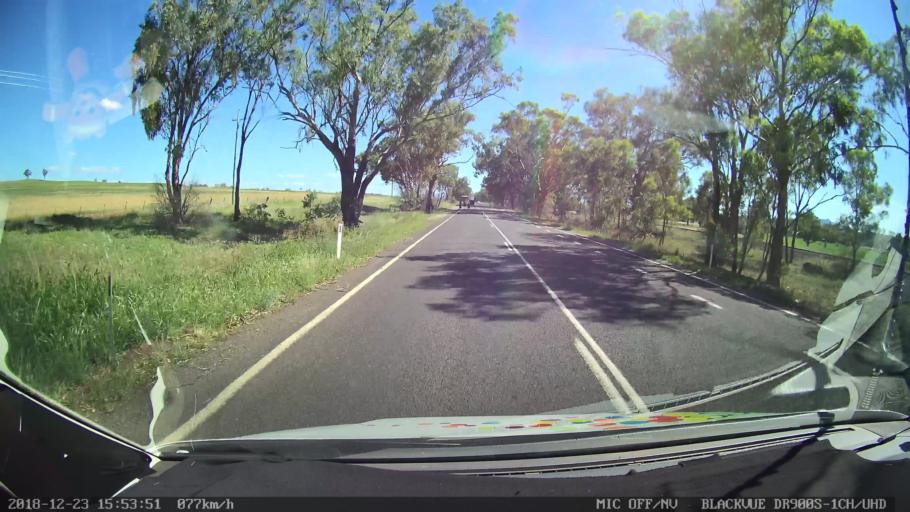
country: AU
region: New South Wales
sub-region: Tamworth Municipality
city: Phillip
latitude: -31.1383
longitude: 150.8789
